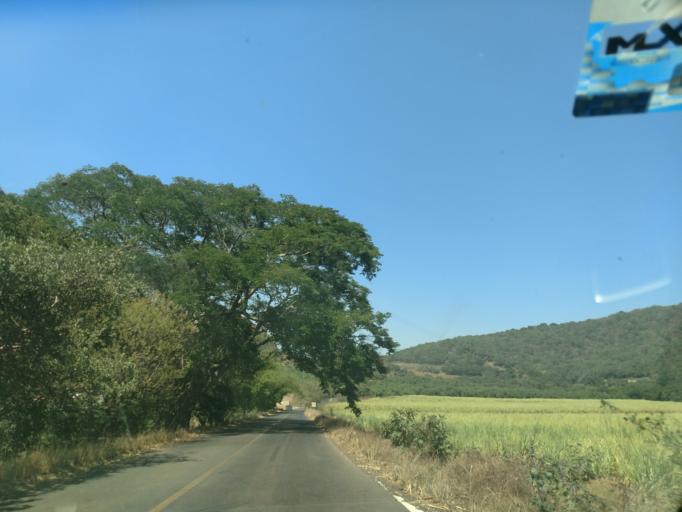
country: MX
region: Nayarit
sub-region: Tepic
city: La Corregidora
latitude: 21.4983
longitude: -104.7793
